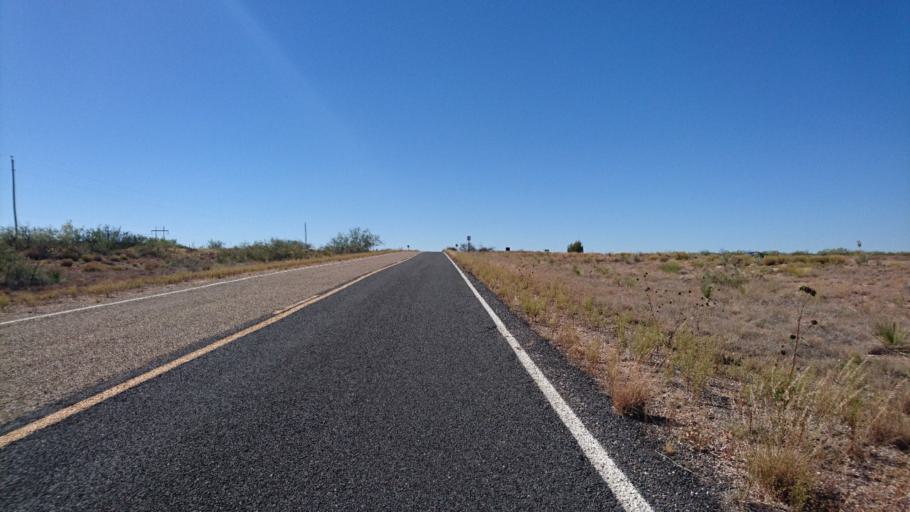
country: US
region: New Mexico
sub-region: Quay County
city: Tucumcari
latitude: 35.0801
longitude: -104.1223
